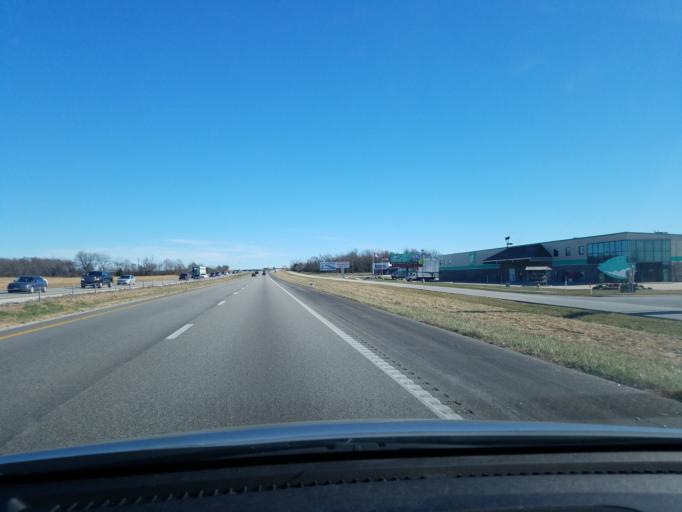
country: US
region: Missouri
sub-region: Greene County
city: Strafford
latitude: 37.2501
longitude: -93.1969
